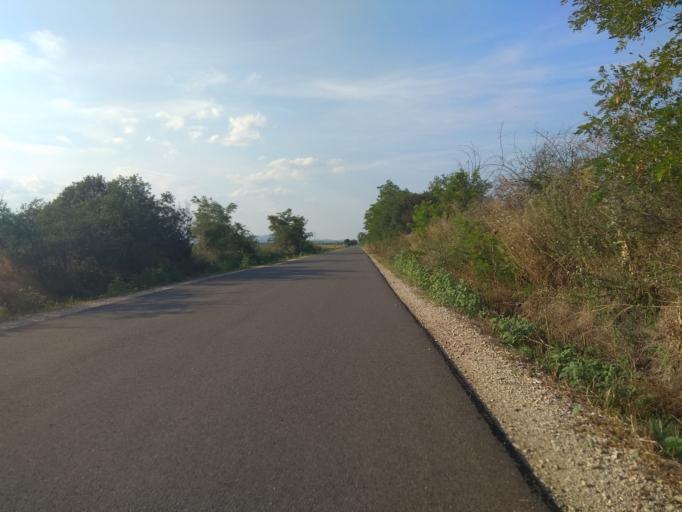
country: HU
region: Borsod-Abauj-Zemplen
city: Harsany
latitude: 47.9037
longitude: 20.7442
